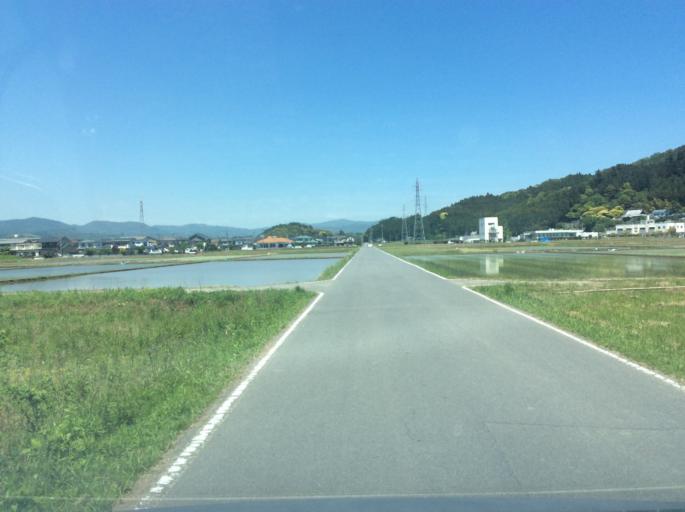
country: JP
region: Fukushima
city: Iwaki
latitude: 37.0740
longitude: 140.8866
